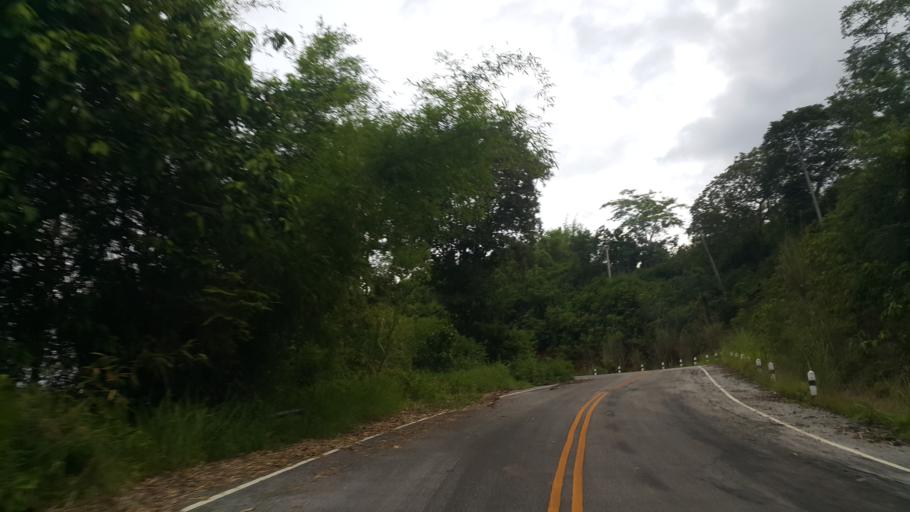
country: TH
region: Loei
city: Na Haeo
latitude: 17.4759
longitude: 101.1142
